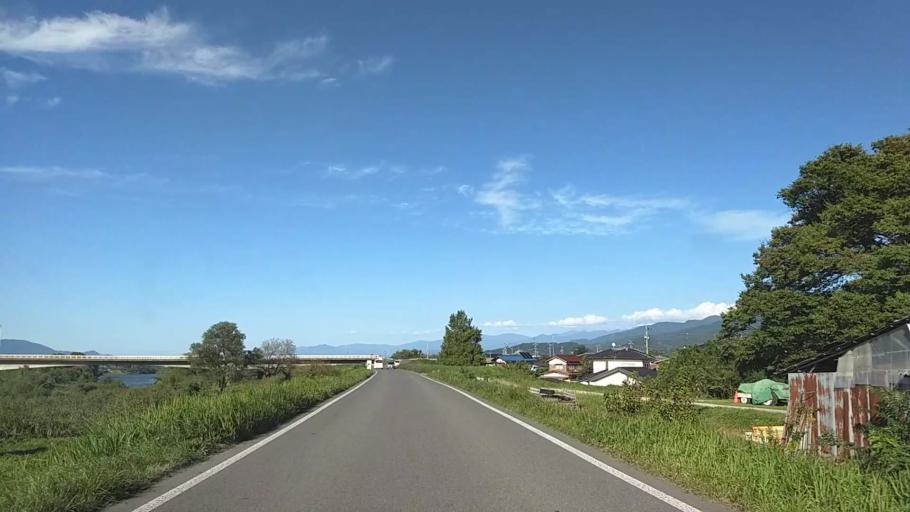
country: JP
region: Nagano
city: Nagano-shi
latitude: 36.5596
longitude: 138.1570
